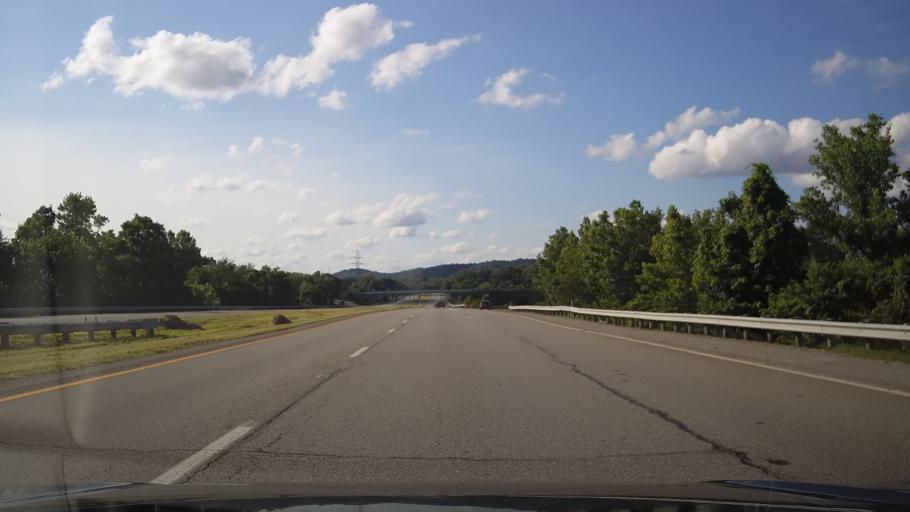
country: US
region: Ohio
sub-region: Lawrence County
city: Coal Grove
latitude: 38.4959
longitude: -82.6483
